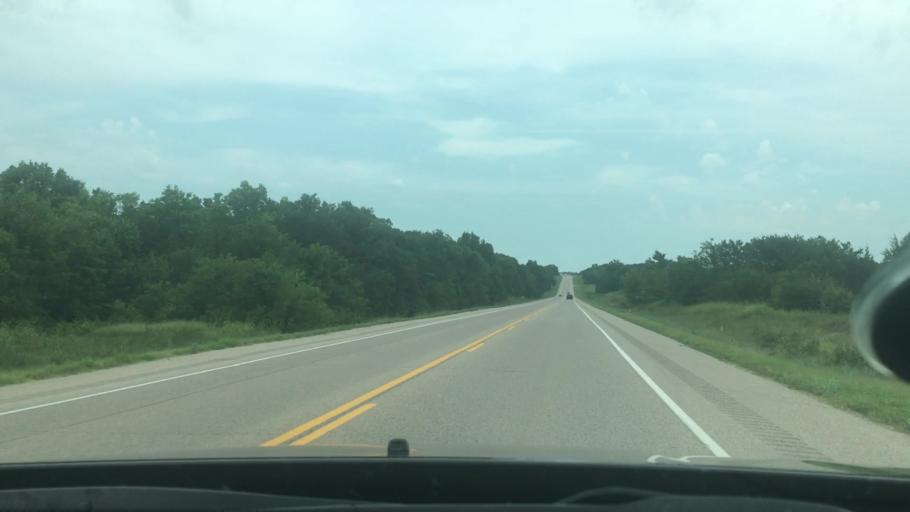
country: US
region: Oklahoma
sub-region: Seminole County
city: Konawa
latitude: 35.0023
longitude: -96.6789
